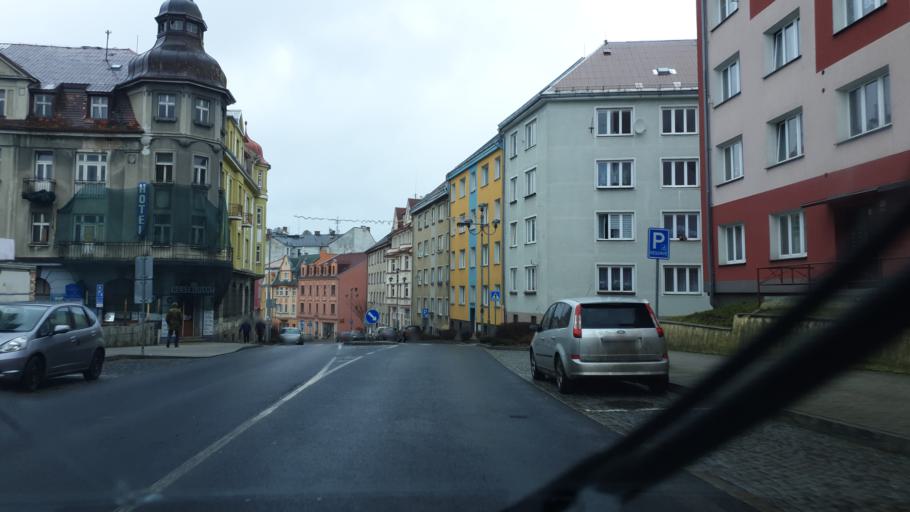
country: CZ
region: Karlovarsky
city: As
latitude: 50.2167
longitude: 12.1953
